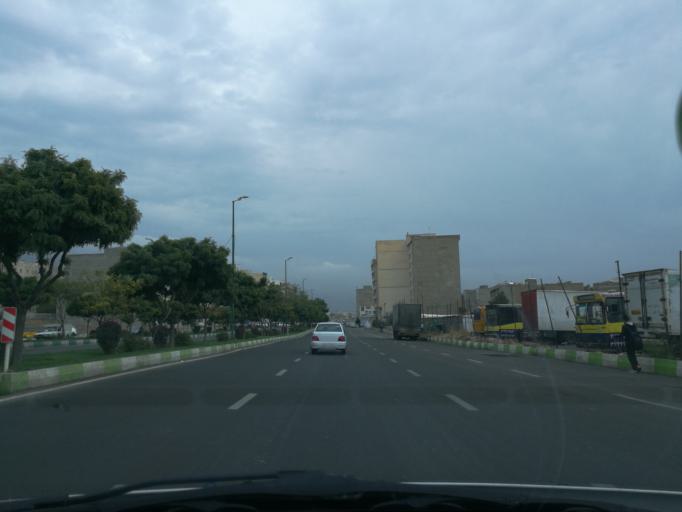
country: IR
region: Alborz
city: Karaj
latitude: 35.8534
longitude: 50.9604
